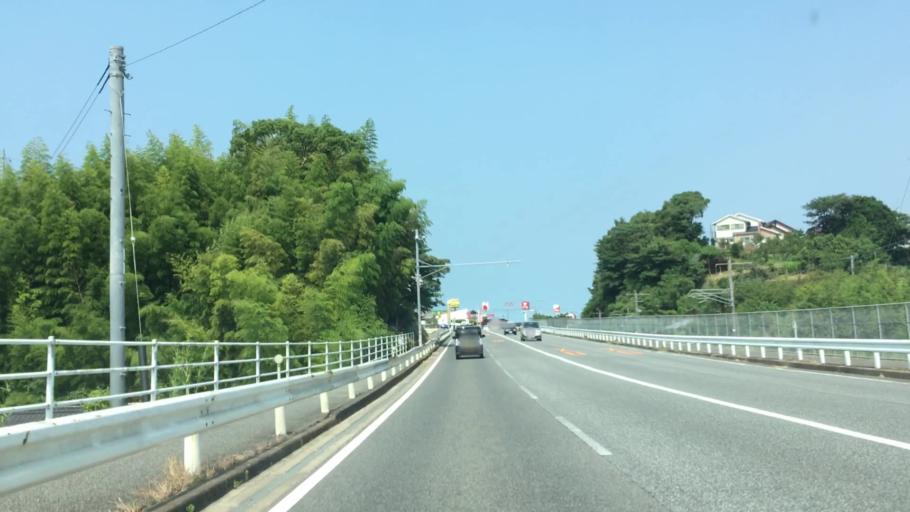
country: JP
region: Nagasaki
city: Sasebo
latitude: 33.1419
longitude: 129.7925
